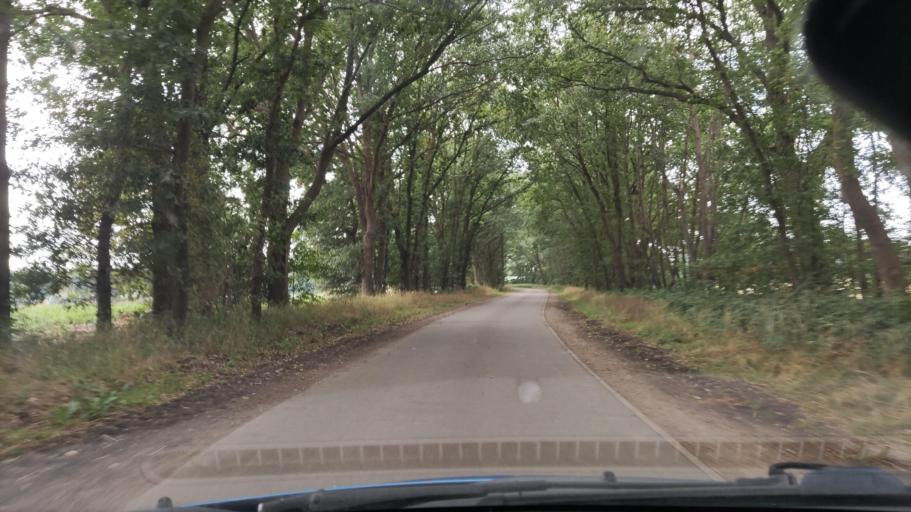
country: DE
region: Lower Saxony
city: Wittorf
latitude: 53.3402
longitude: 10.3743
